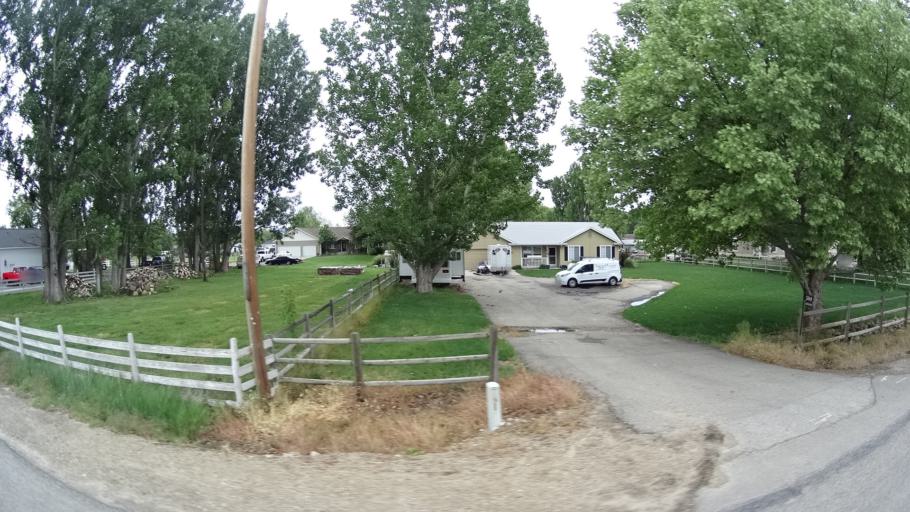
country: US
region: Idaho
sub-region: Ada County
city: Star
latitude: 43.6869
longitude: -116.4932
